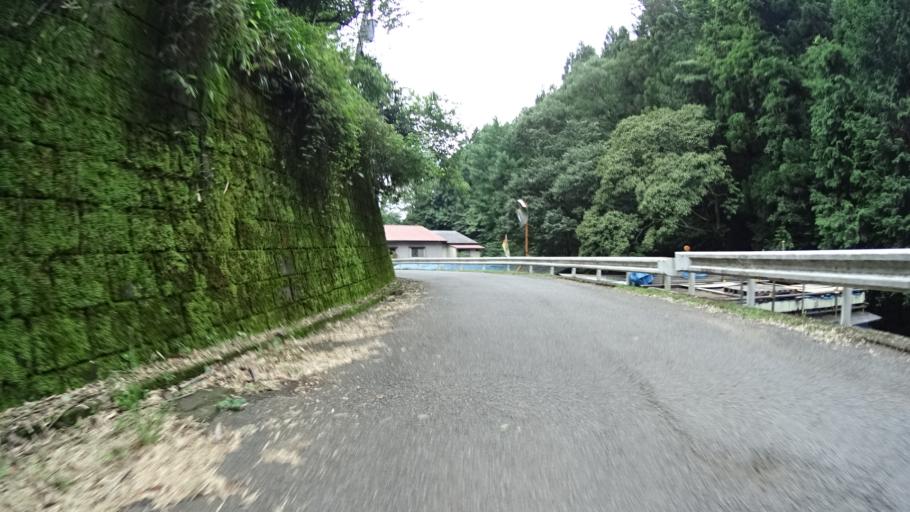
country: JP
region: Kanagawa
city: Atsugi
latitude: 35.4979
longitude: 139.2669
